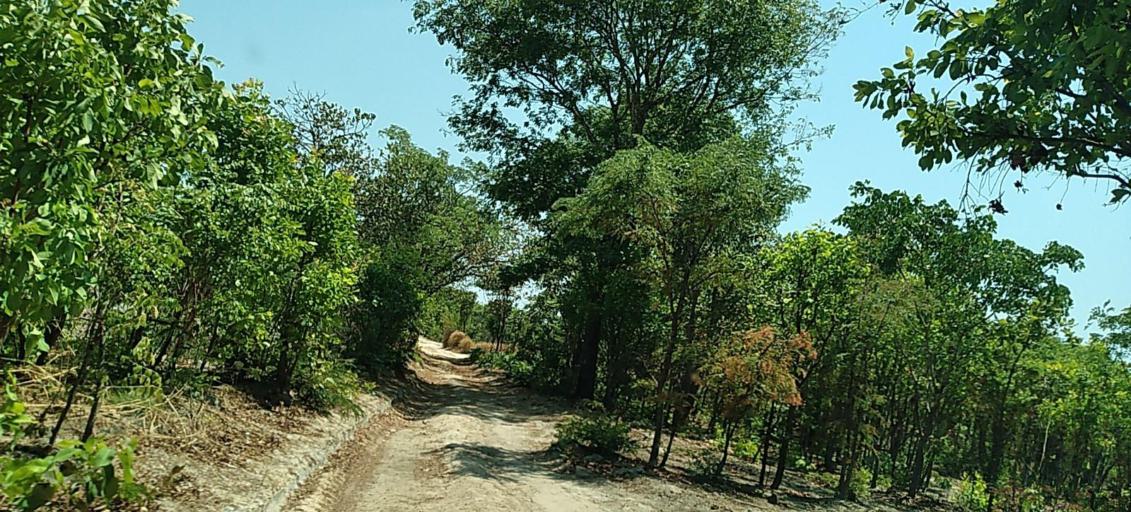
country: ZM
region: Copperbelt
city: Luanshya
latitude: -12.9833
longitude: 28.3294
